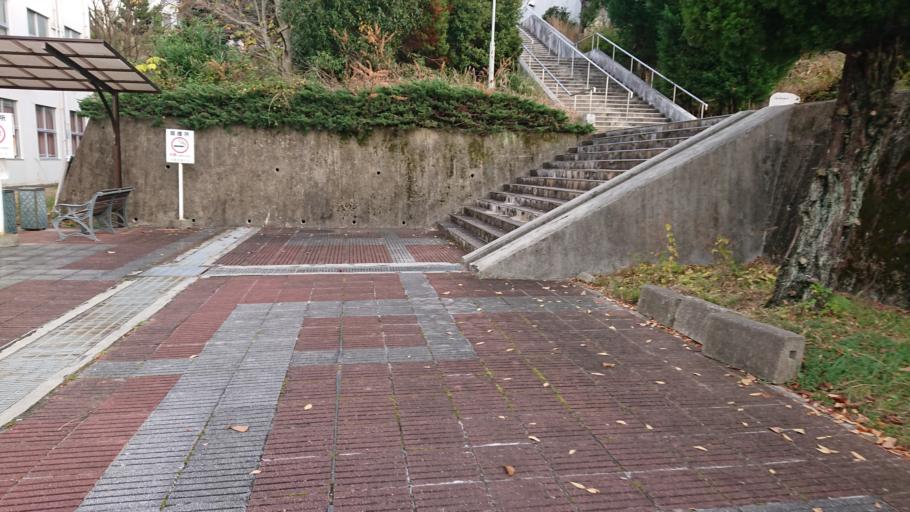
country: JP
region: Kyoto
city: Kameoka
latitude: 34.9942
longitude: 135.5534
